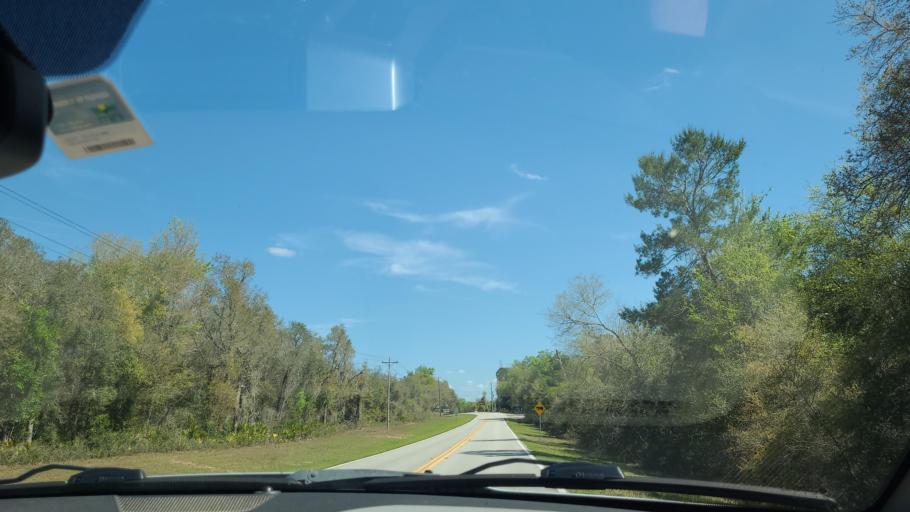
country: US
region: Florida
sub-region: Putnam County
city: Crescent City
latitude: 29.3760
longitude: -81.7520
